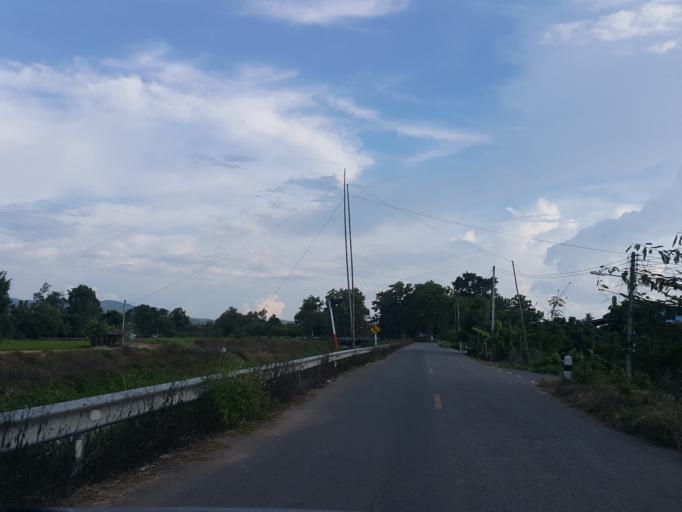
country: TH
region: Chiang Mai
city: Mae Taeng
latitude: 19.0471
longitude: 98.9761
